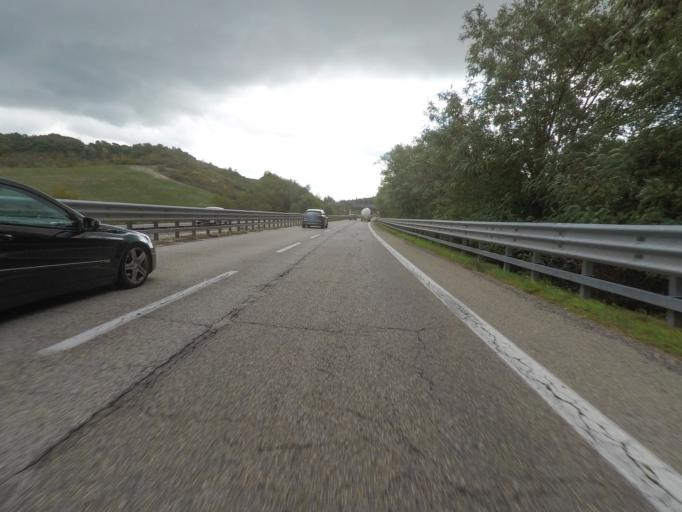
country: IT
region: Tuscany
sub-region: Provincia di Siena
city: Rapolano Terme
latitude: 43.3134
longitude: 11.5784
